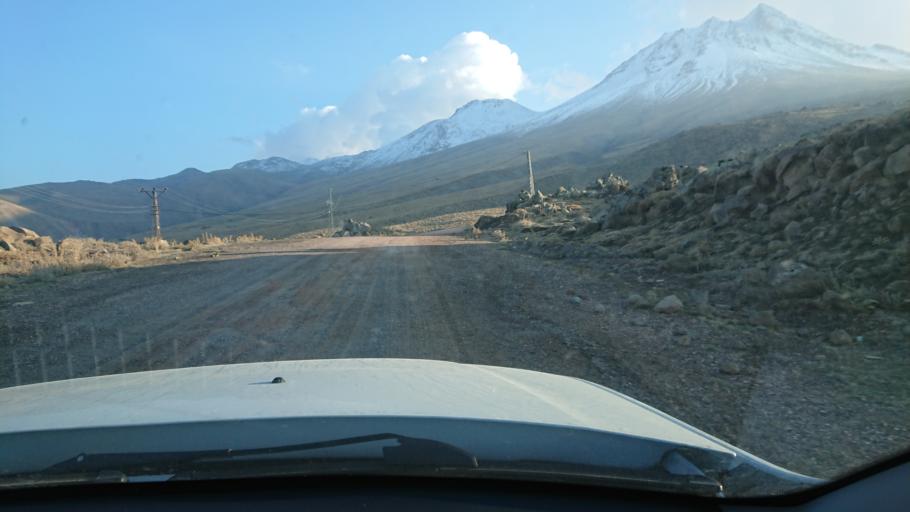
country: TR
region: Aksaray
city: Taspinar
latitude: 38.1603
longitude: 34.1653
